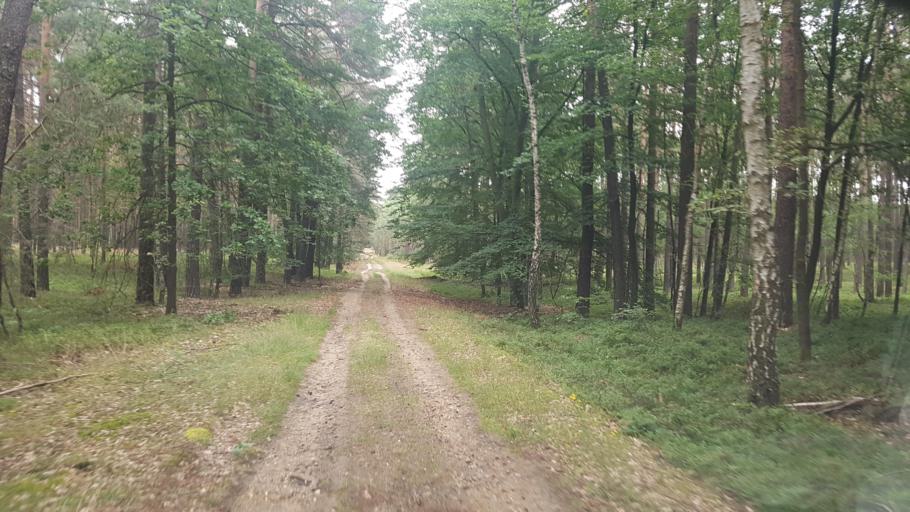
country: DE
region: Brandenburg
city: Crinitz
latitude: 51.7362
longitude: 13.7991
